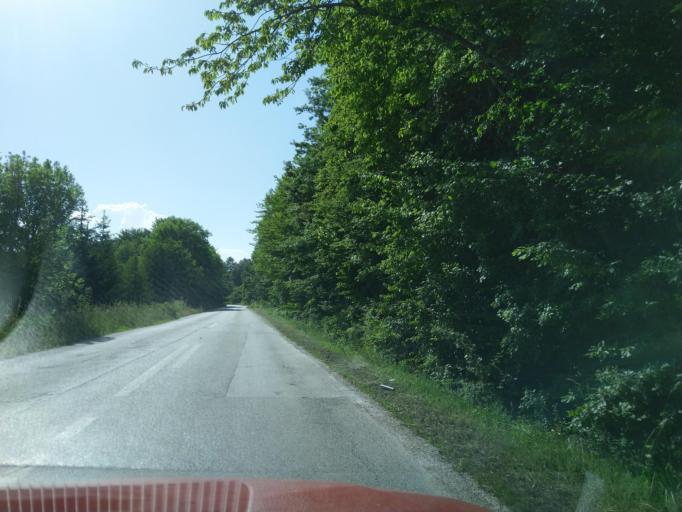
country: RS
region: Central Serbia
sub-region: Zlatiborski Okrug
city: Uzice
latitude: 43.8724
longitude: 19.7301
